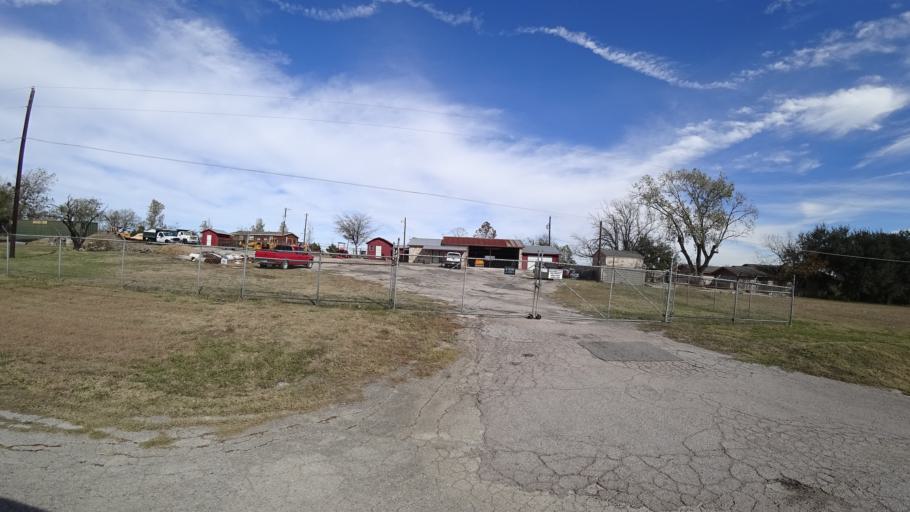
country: US
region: Texas
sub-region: Travis County
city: Onion Creek
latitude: 30.1243
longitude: -97.6885
